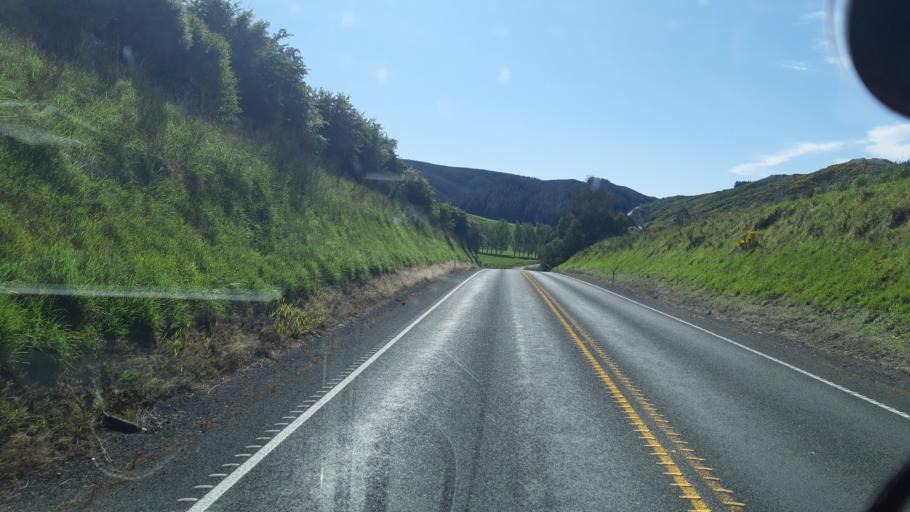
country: NZ
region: Otago
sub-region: Clutha District
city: Balclutha
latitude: -45.8129
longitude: 169.5106
